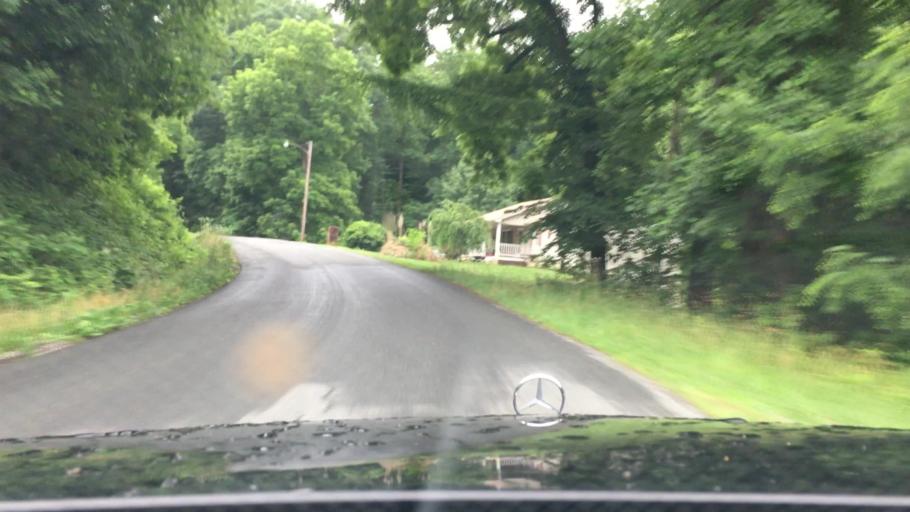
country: US
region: Virginia
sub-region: Pittsylvania County
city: Hurt
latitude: 37.0989
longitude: -79.3011
